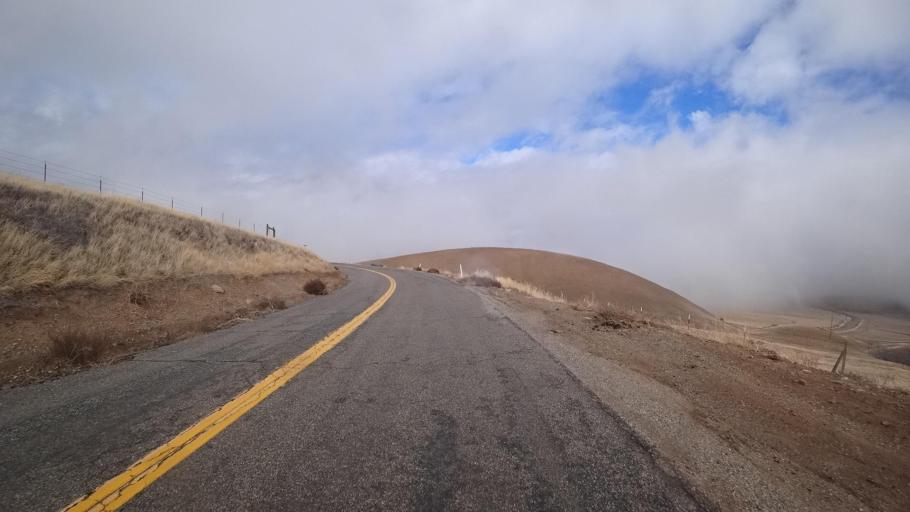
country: US
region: California
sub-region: Kern County
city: Maricopa
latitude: 34.9298
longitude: -119.4085
